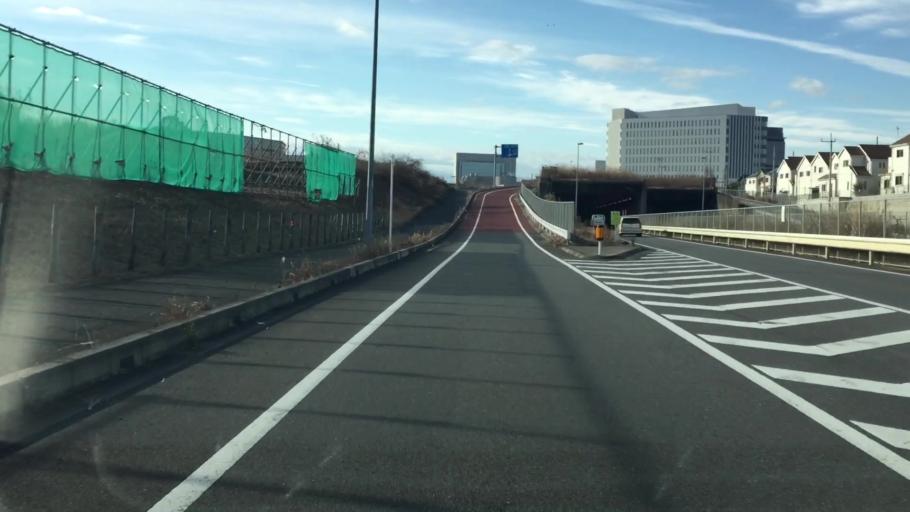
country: JP
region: Chiba
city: Shiroi
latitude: 35.8135
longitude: 140.1266
